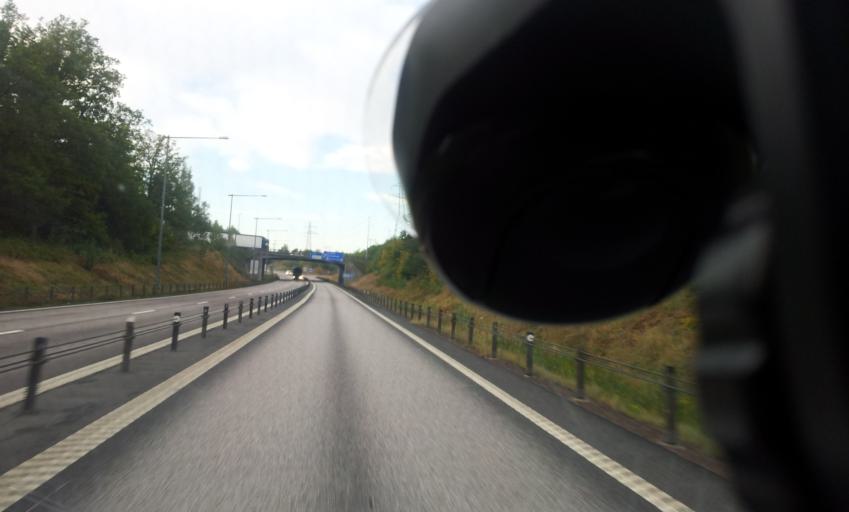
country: SE
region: Kalmar
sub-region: Oskarshamns Kommun
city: Oskarshamn
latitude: 57.2667
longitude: 16.4308
